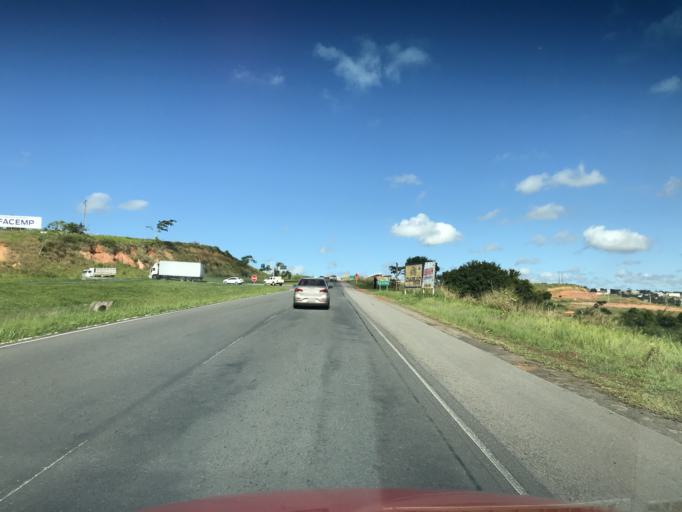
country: BR
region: Bahia
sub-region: Santo Antonio De Jesus
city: Santo Antonio de Jesus
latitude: -12.9502
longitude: -39.2536
